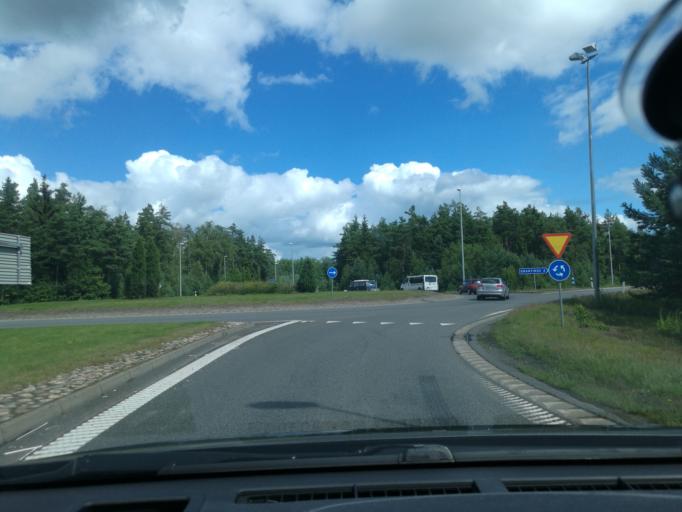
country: SE
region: Skane
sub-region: Hassleholms Kommun
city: Hassleholm
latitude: 56.1692
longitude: 13.8340
